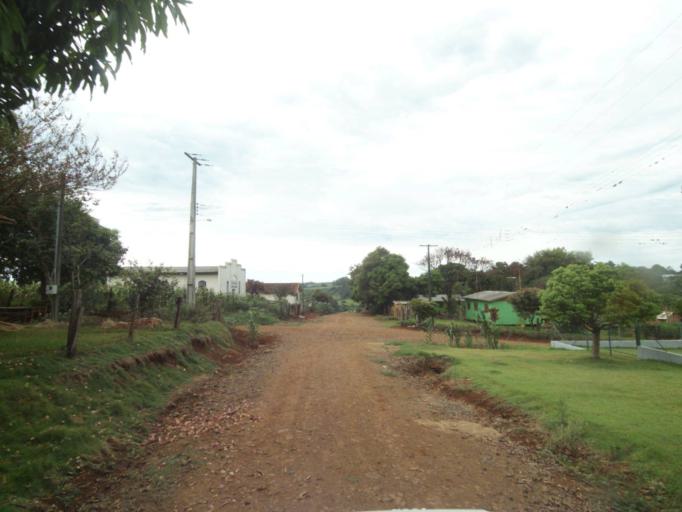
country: BR
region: Parana
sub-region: Guaraniacu
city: Guaraniacu
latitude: -24.9209
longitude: -52.9414
